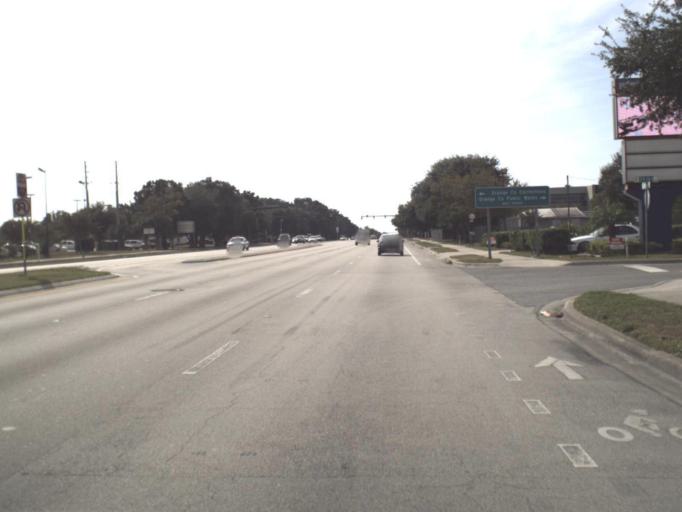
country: US
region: Florida
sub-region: Orange County
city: Holden Heights
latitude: 28.5037
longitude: -81.4176
